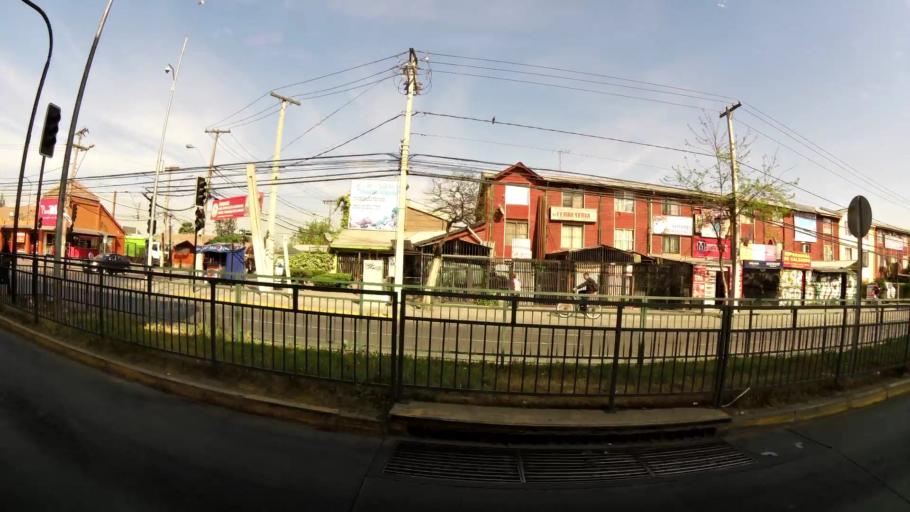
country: CL
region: Santiago Metropolitan
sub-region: Provincia de Cordillera
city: Puente Alto
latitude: -33.5687
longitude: -70.5841
